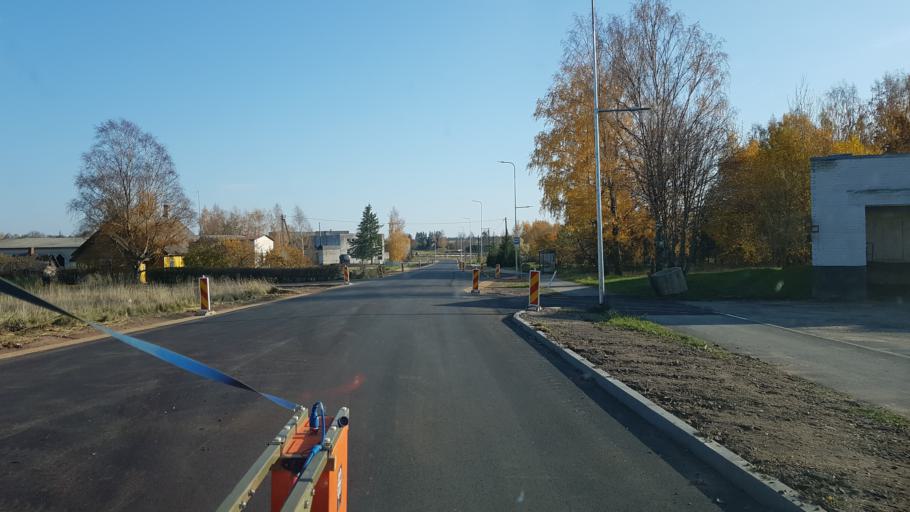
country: EE
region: Vorumaa
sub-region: Antsla vald
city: Vana-Antsla
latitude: 57.8419
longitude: 26.4782
